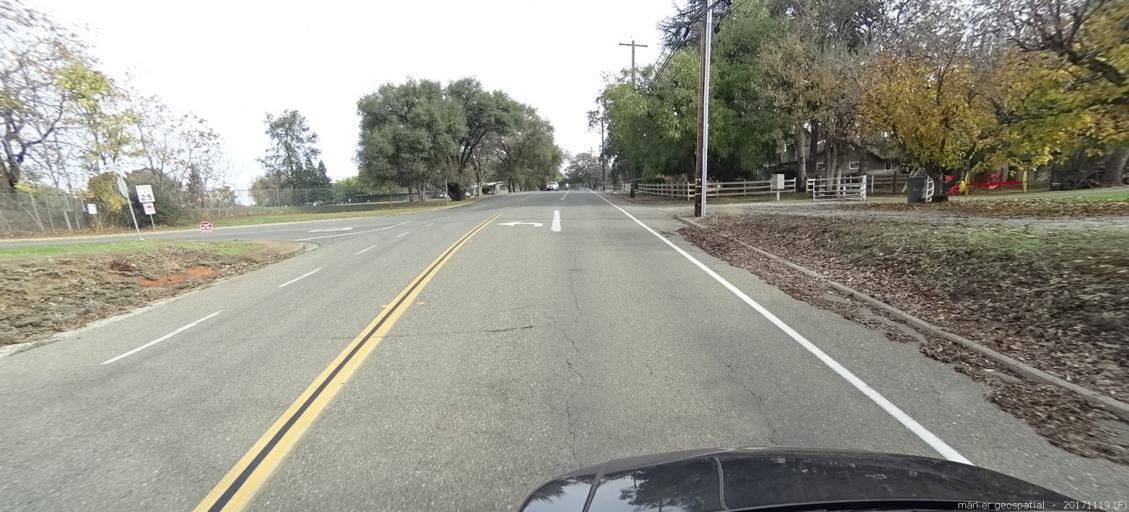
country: US
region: California
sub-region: Shasta County
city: Anderson
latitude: 40.4812
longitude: -122.3039
